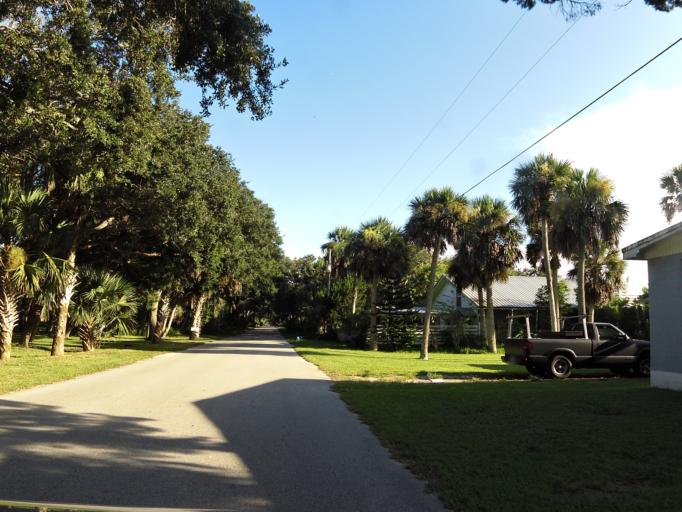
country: US
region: Florida
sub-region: Flagler County
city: Flagler Beach
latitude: 29.4674
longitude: -81.1246
